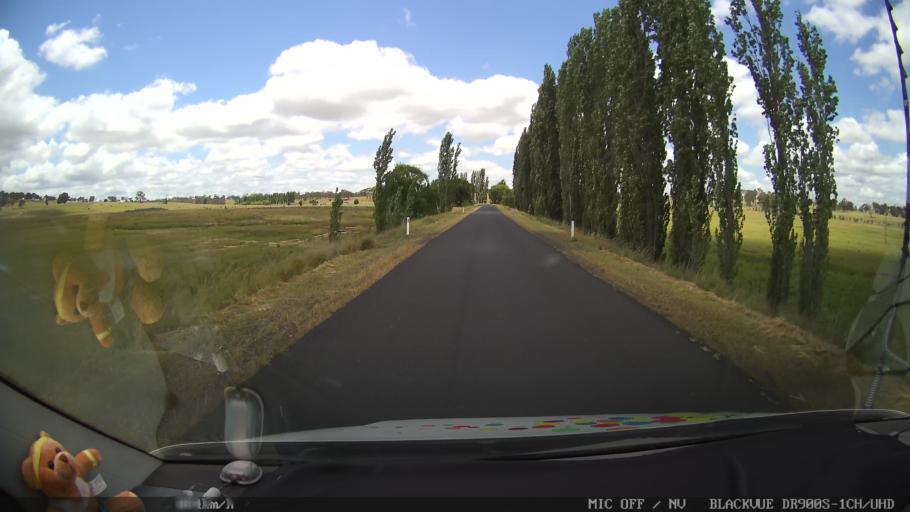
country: AU
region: New South Wales
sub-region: Glen Innes Severn
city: Glen Innes
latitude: -29.4337
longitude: 151.7548
